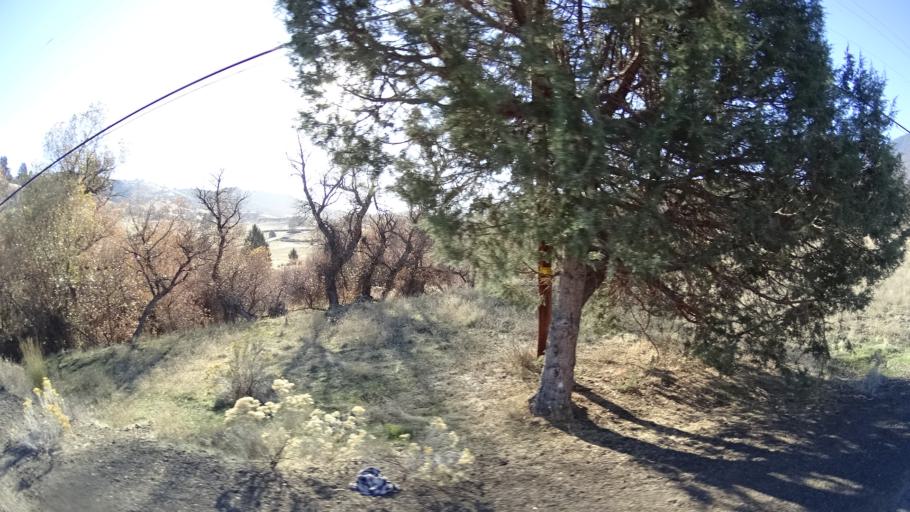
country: US
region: California
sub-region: Siskiyou County
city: Montague
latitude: 41.8900
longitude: -122.4822
